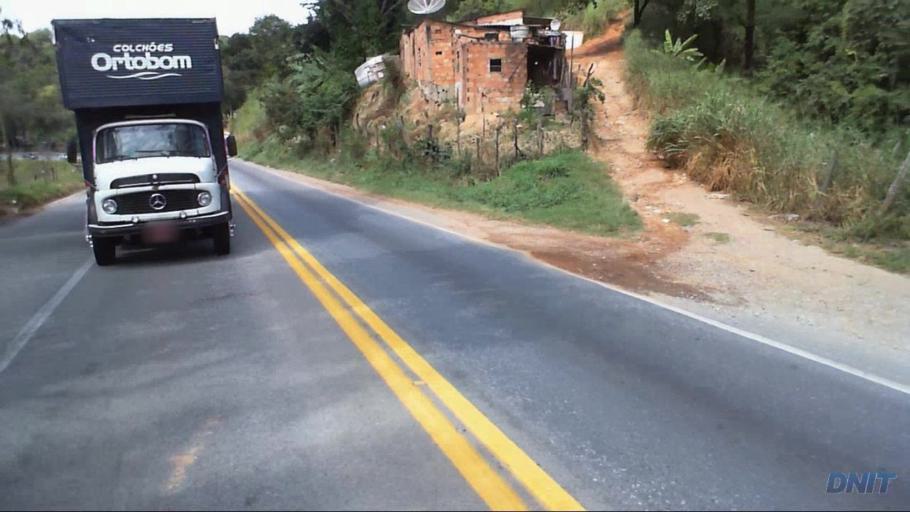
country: BR
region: Minas Gerais
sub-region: Santa Luzia
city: Santa Luzia
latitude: -19.8248
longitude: -43.8217
